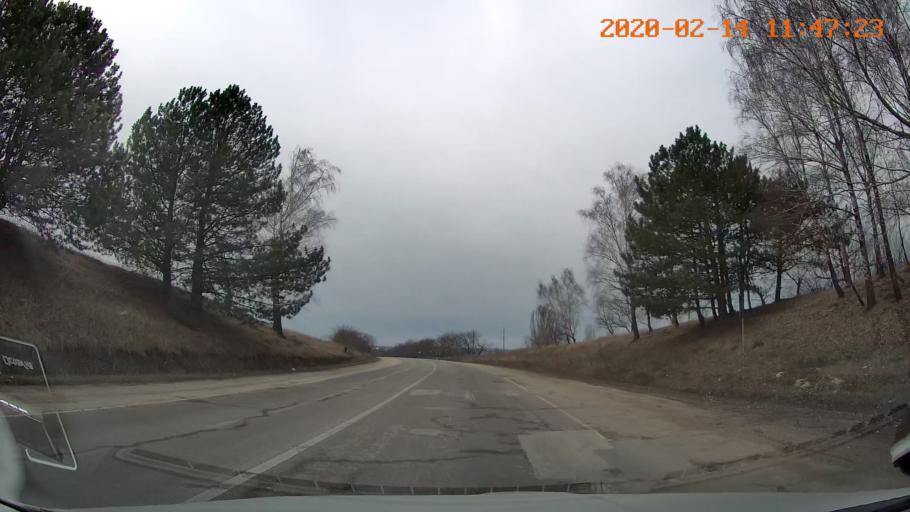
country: MD
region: Briceni
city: Briceni
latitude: 48.3165
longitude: 26.9711
